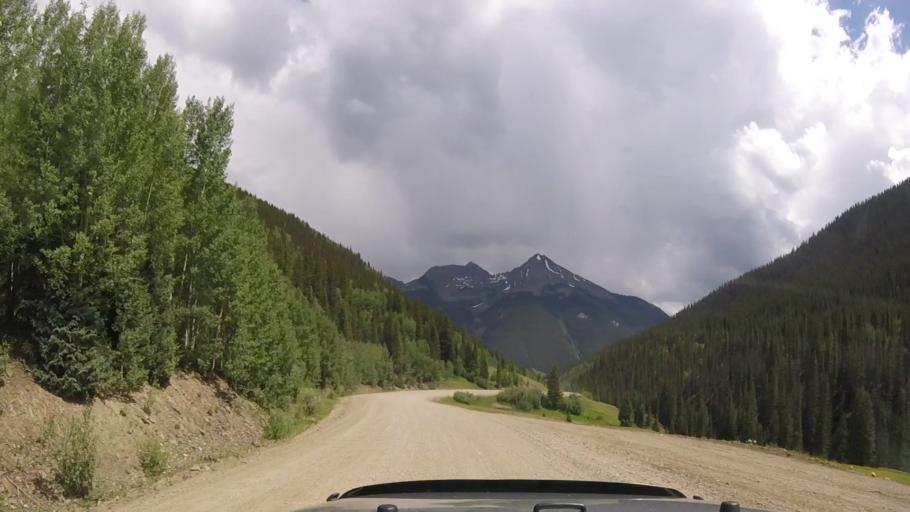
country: US
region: Colorado
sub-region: San Juan County
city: Silverton
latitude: 37.8289
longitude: -107.6701
